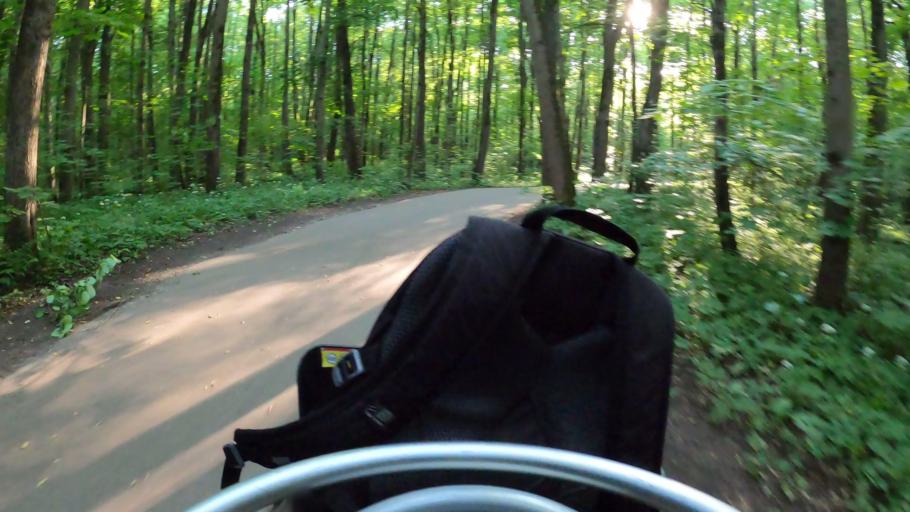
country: RU
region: Moscow
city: Zyuzino
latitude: 55.6225
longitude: 37.5697
